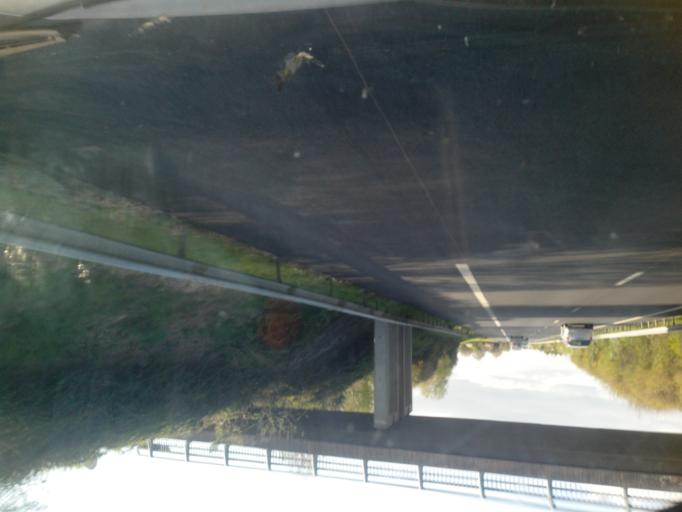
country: FR
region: Pays de la Loire
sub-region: Departement de la Loire-Atlantique
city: La Grigonnais
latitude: 47.4903
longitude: -1.6380
